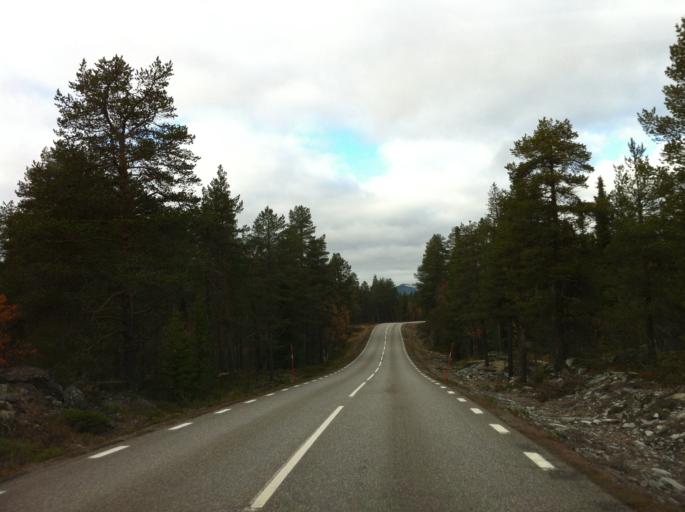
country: NO
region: Hedmark
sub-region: Engerdal
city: Engerdal
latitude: 62.0445
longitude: 12.3434
